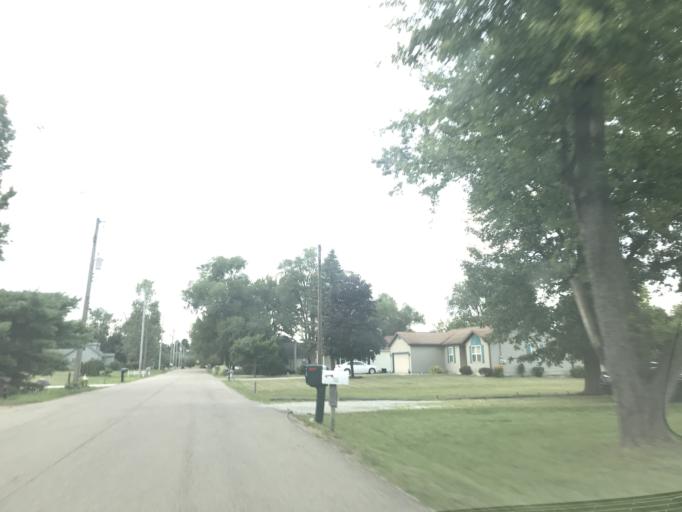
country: US
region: Michigan
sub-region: Eaton County
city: Waverly
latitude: 42.7159
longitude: -84.6264
